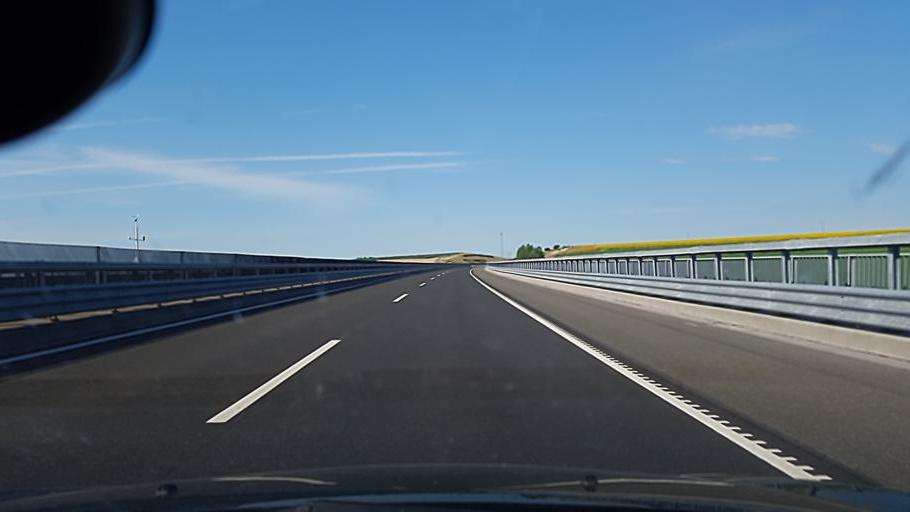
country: HU
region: Tolna
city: Paks
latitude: 46.7067
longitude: 18.8710
